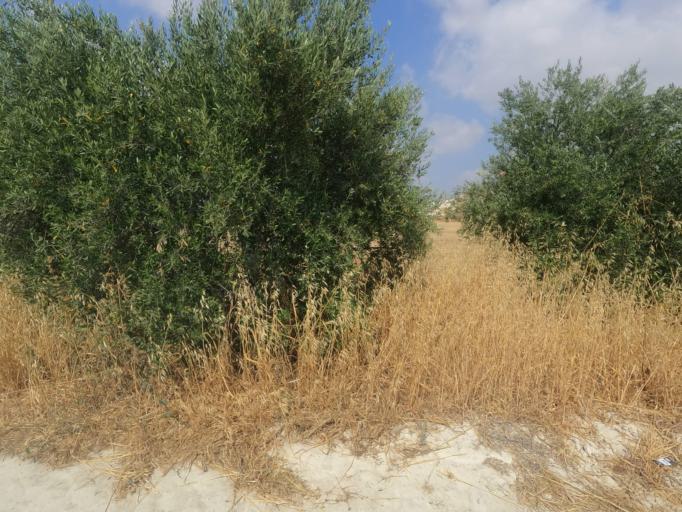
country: CY
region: Larnaka
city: Aradippou
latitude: 34.9379
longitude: 33.5509
